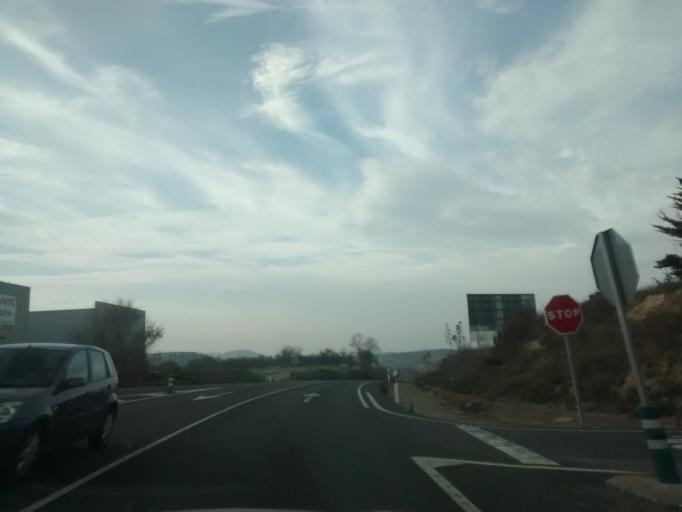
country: ES
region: La Rioja
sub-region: Provincia de La Rioja
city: Briones
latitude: 42.5420
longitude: -2.7882
